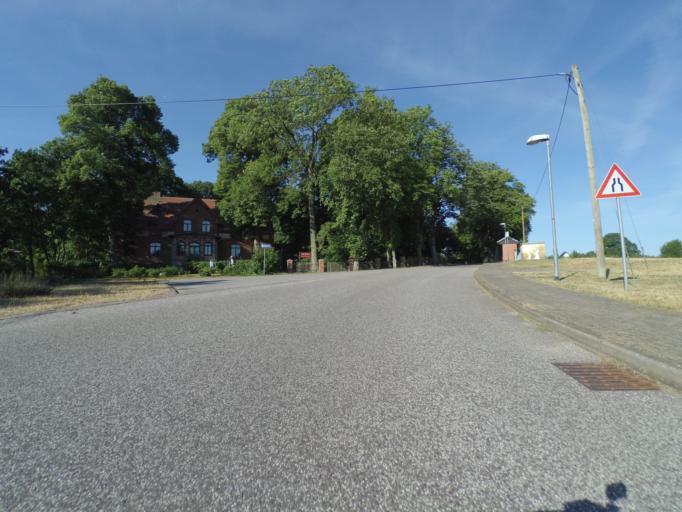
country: DE
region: Brandenburg
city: Gerdshagen
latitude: 53.3729
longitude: 12.1481
